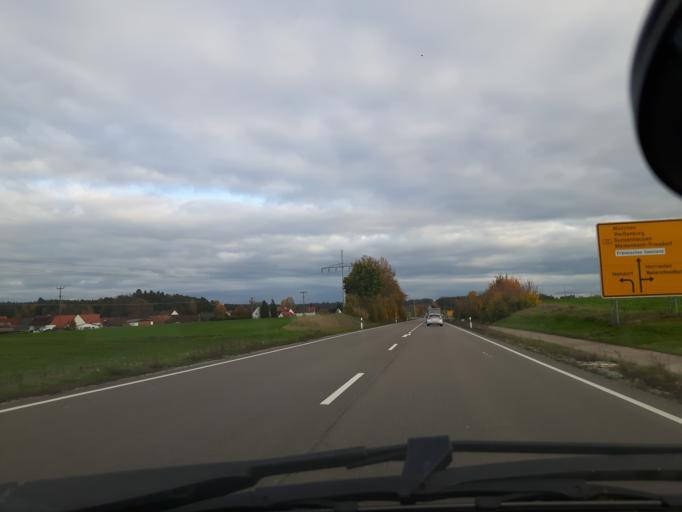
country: DE
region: Bavaria
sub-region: Regierungsbezirk Mittelfranken
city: Burgoberbach
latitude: 49.2330
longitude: 10.6182
